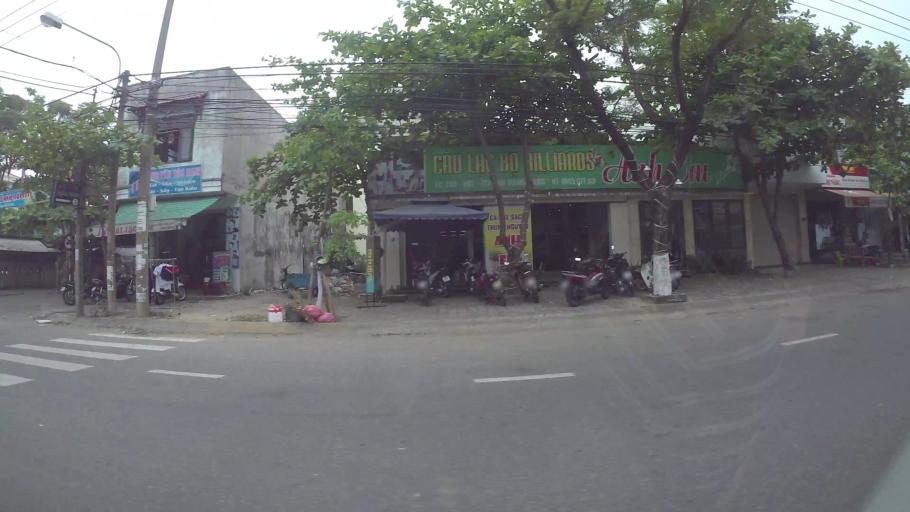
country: VN
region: Da Nang
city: Lien Chieu
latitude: 16.0774
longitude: 108.1654
